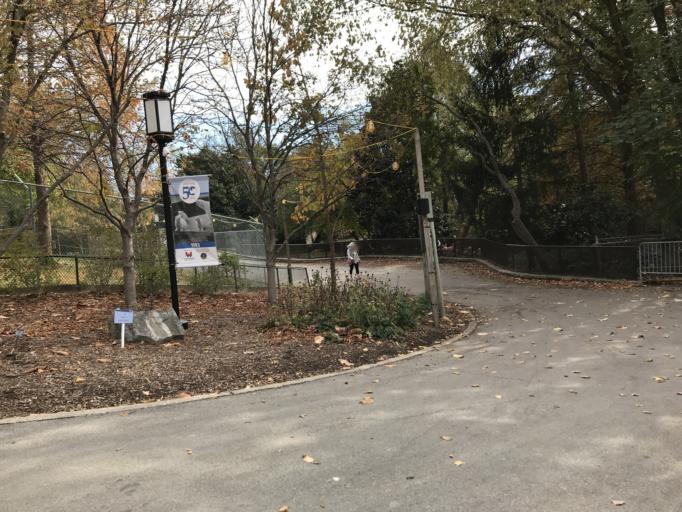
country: US
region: Kentucky
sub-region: Jefferson County
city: Audubon Park
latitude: 38.2043
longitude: -85.7054
